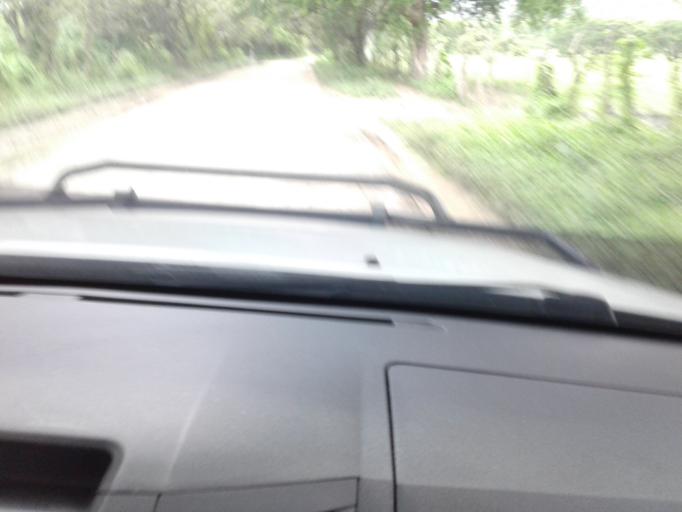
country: NI
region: Matagalpa
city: Ciudad Dario
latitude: 12.9098
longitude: -86.1976
